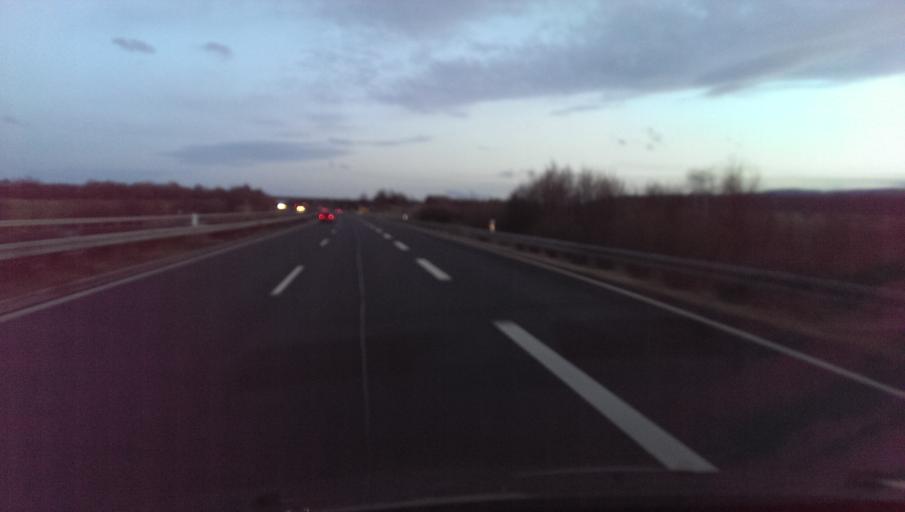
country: DE
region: Saxony-Anhalt
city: Stapelburg
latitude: 51.9070
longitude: 10.6763
